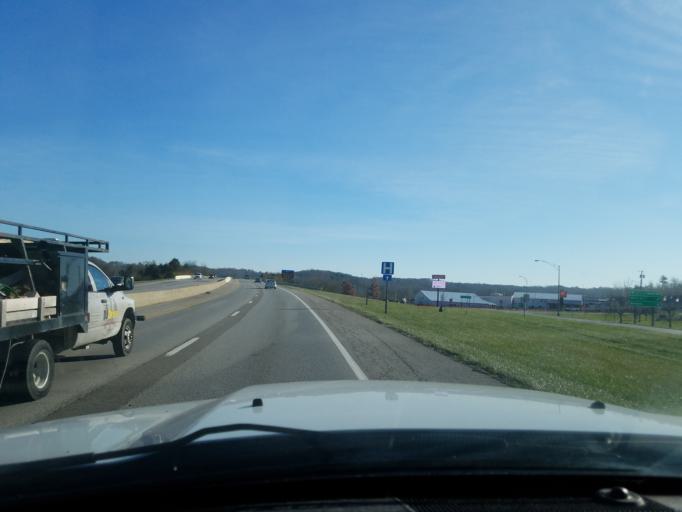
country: US
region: Ohio
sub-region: Clermont County
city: Batavia
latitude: 39.0838
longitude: -84.1905
